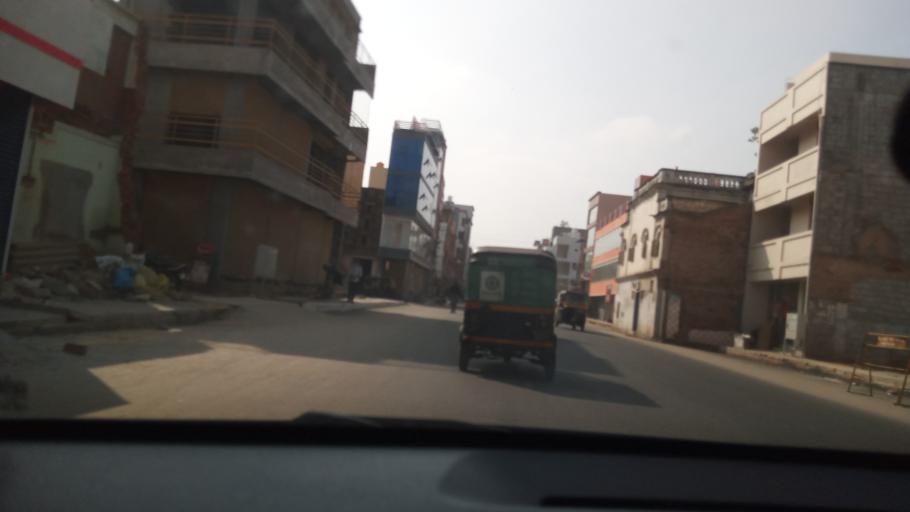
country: IN
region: Karnataka
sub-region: Mysore
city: Mysore
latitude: 12.3143
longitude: 76.6545
